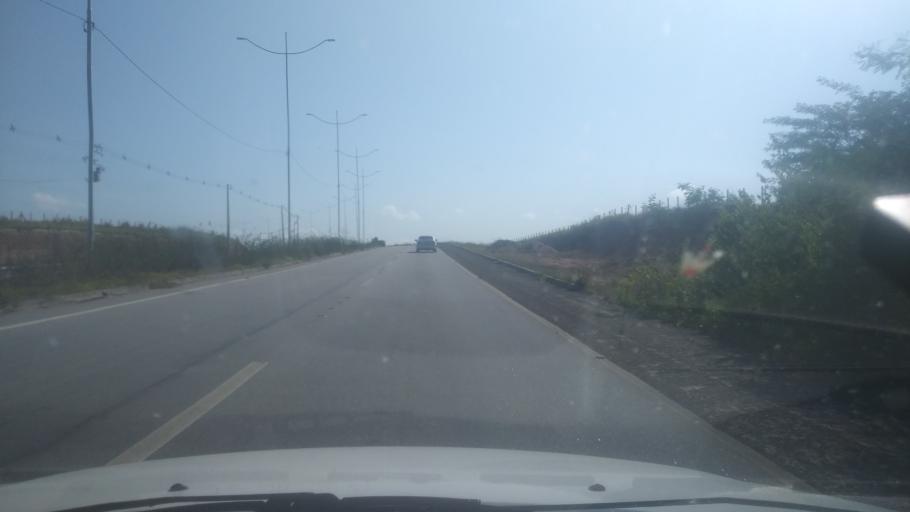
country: BR
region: Rio Grande do Norte
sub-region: Macaiba
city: Macaiba
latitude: -5.8325
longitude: -35.3714
